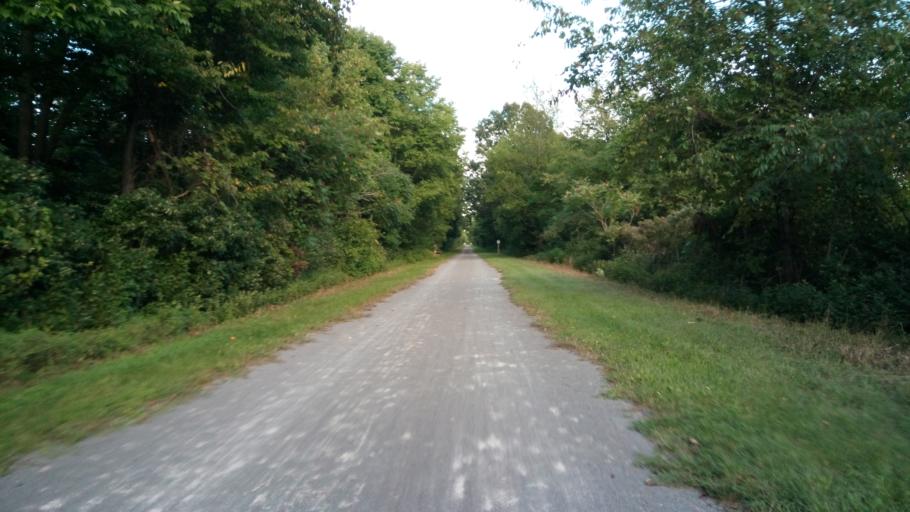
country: US
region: New York
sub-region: Ontario County
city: Victor
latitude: 43.0013
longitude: -77.4625
